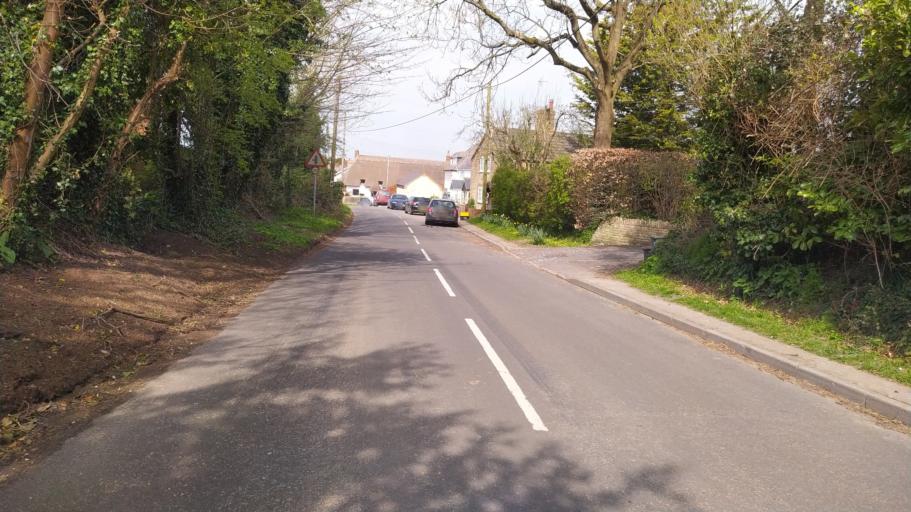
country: GB
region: England
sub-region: Borough of Swindon
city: Wanborough
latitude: 51.5479
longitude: -1.6932
